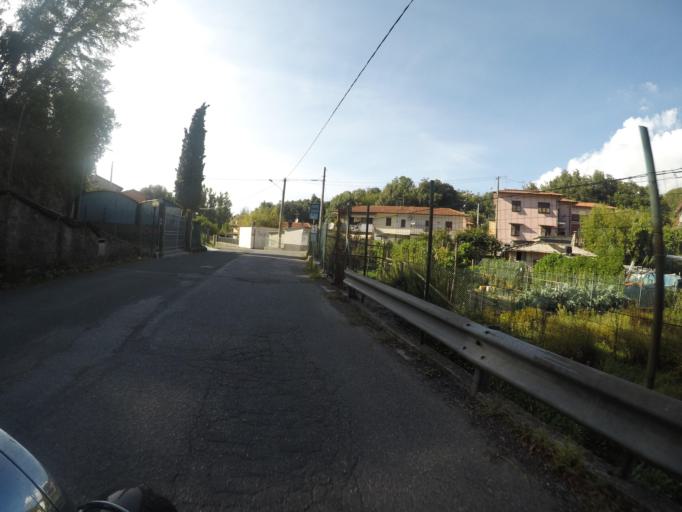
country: IT
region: Tuscany
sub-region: Provincia di Massa-Carrara
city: Massa
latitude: 44.0646
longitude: 10.1252
